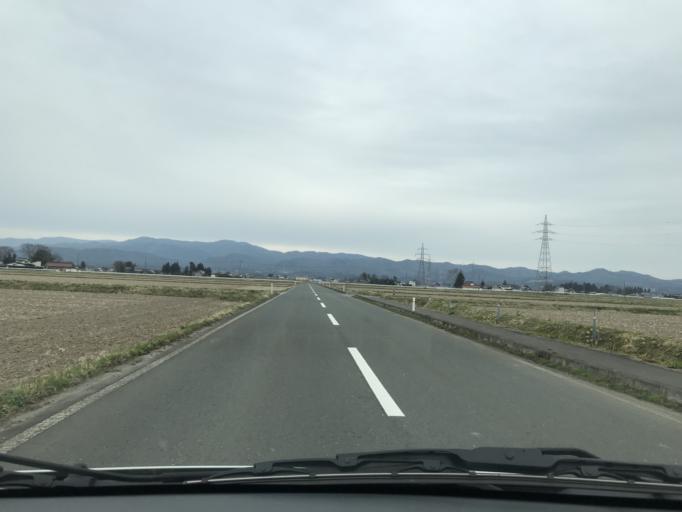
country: JP
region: Iwate
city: Mizusawa
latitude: 39.0861
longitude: 141.1408
